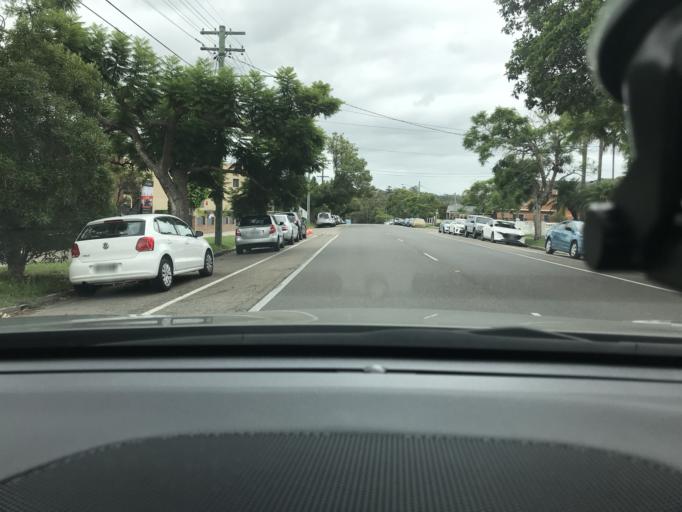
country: AU
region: New South Wales
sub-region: Canada Bay
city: Wareemba
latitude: -33.8468
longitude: 151.1284
